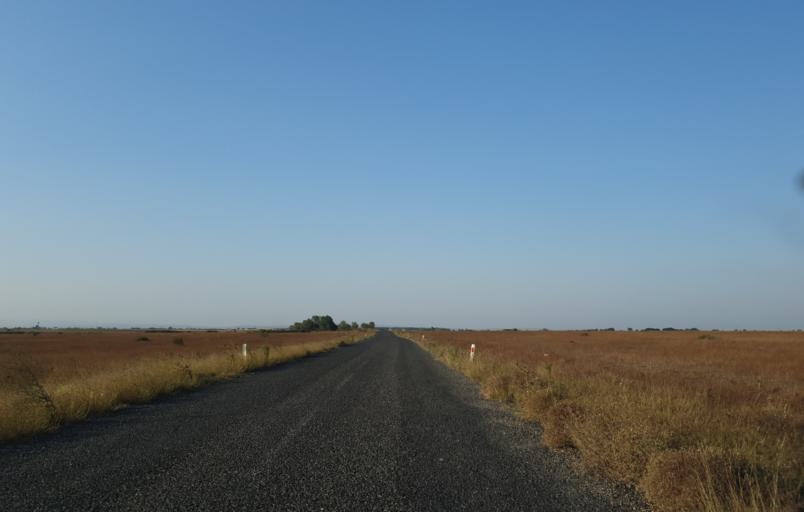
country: TR
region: Tekirdag
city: Beyazkoy
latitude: 41.4100
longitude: 27.7615
